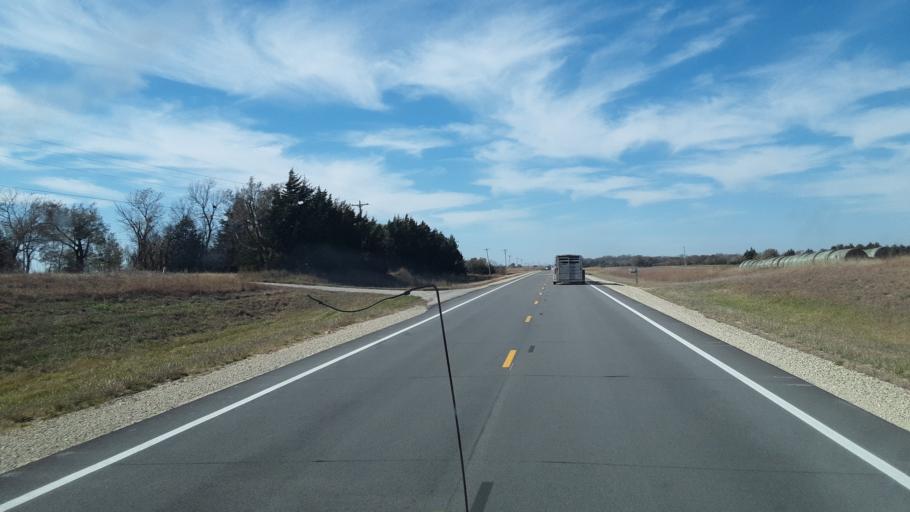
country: US
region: Kansas
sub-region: Marion County
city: Marion
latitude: 38.3628
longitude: -96.9436
